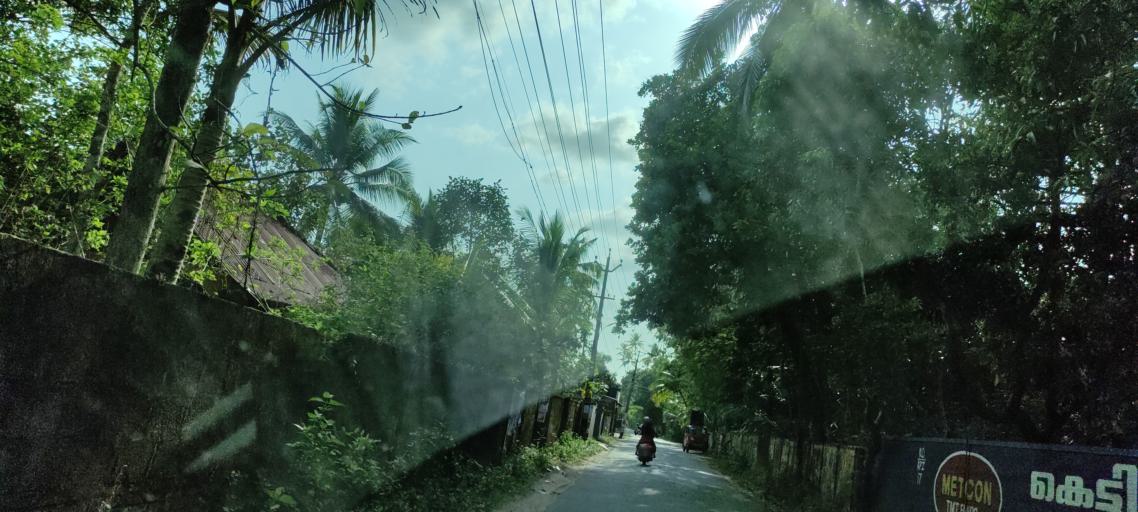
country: IN
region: Kerala
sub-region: Alappuzha
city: Vayalar
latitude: 9.6867
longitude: 76.3084
